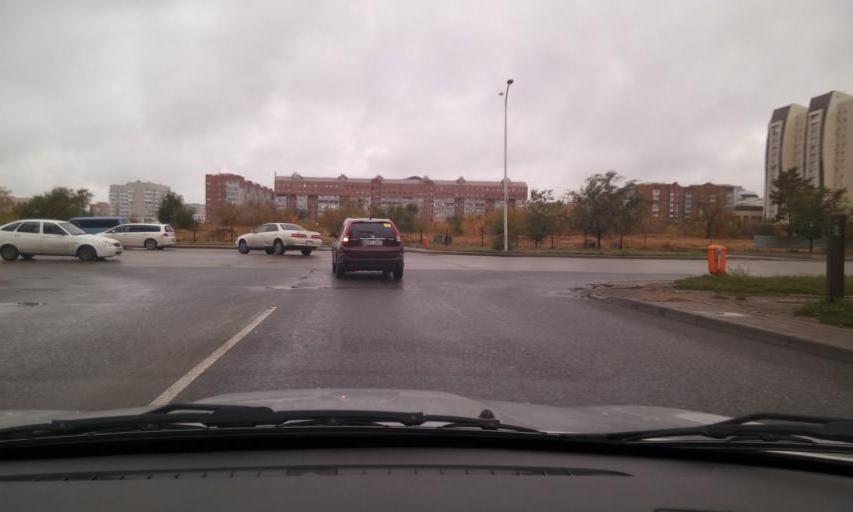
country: KZ
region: Astana Qalasy
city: Astana
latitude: 51.1620
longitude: 71.4027
